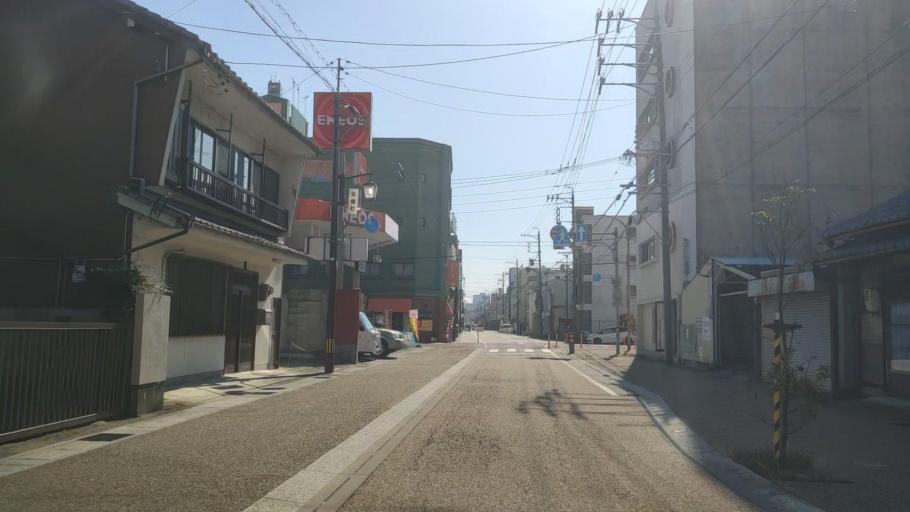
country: JP
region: Gifu
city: Gifu-shi
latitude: 35.4266
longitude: 136.7646
